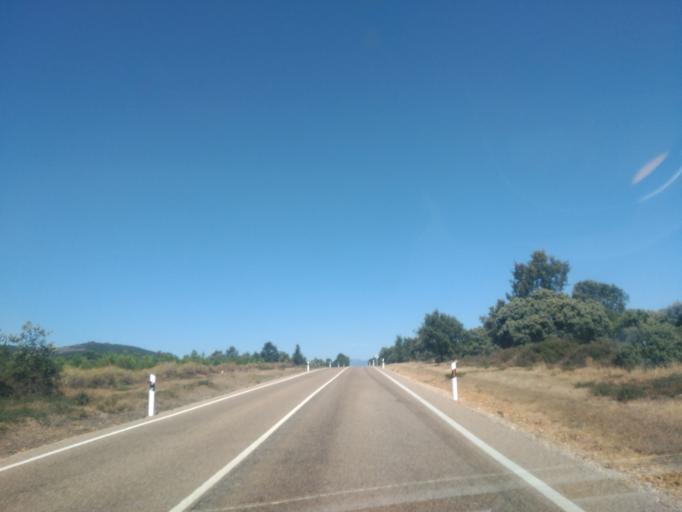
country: ES
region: Castille and Leon
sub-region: Provincia de Zamora
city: Ferreras de Abajo
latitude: 41.9134
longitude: -6.0829
